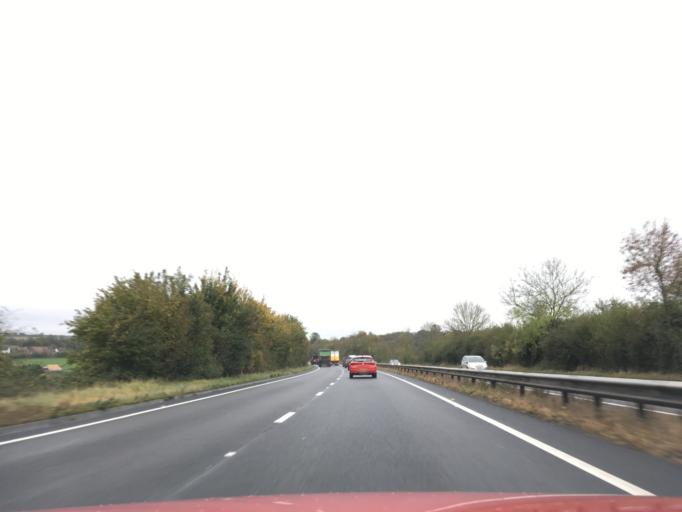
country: GB
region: England
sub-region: Hampshire
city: Overton
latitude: 51.2347
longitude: -1.3484
